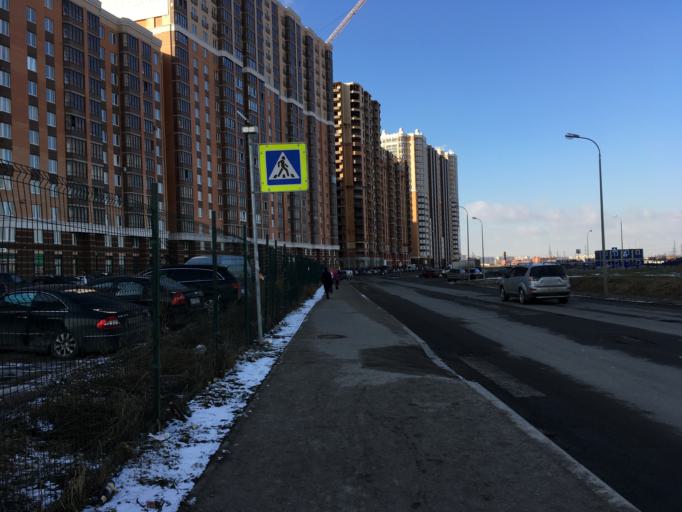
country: RU
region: St.-Petersburg
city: Krasnogvargeisky
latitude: 59.9163
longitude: 30.5205
